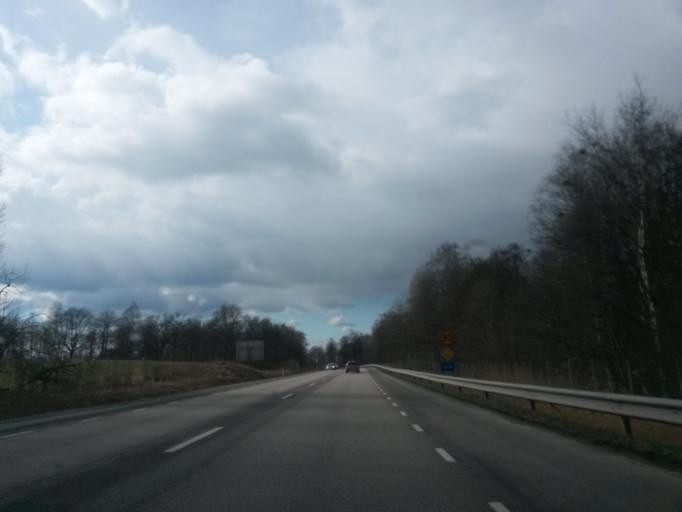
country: SE
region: Vaestra Goetaland
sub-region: Skara Kommun
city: Axvall
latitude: 58.3809
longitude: 13.6831
